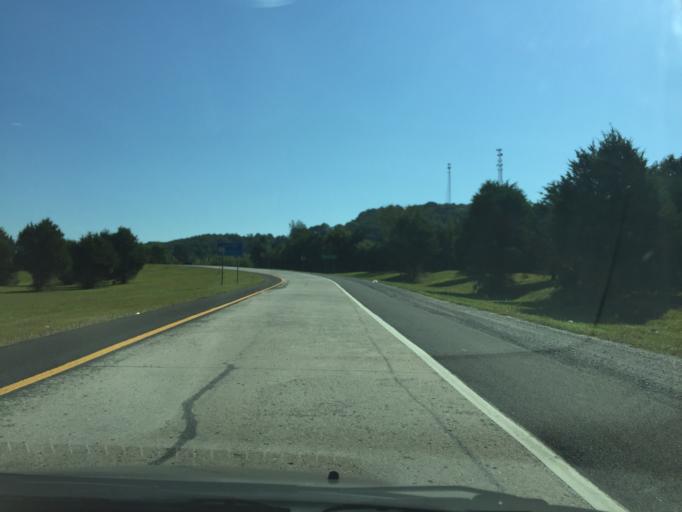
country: US
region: Tennessee
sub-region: Monroe County
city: Sweetwater
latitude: 35.6211
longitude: -84.4919
